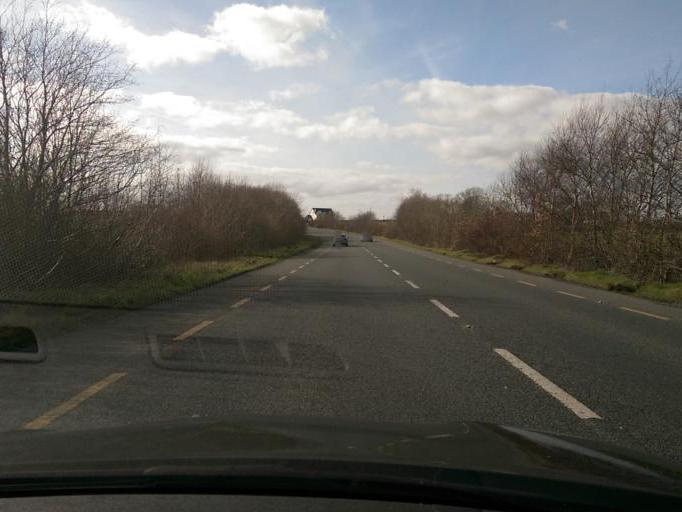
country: IE
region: Connaught
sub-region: County Galway
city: Claregalway
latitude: 53.3034
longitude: -8.9469
